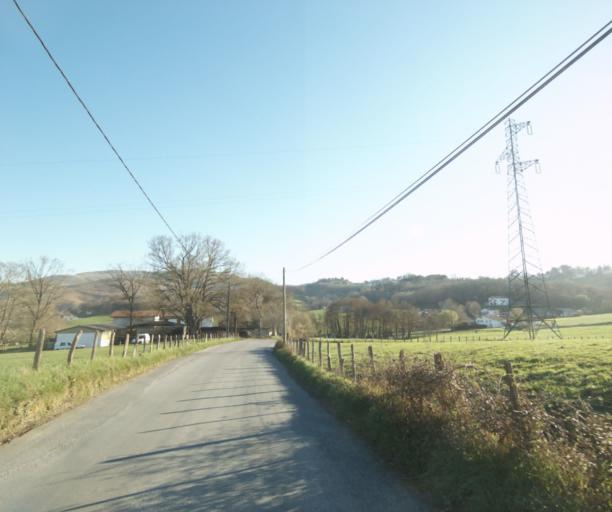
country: FR
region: Aquitaine
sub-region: Departement des Pyrenees-Atlantiques
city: Urrugne
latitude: 43.3562
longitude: -1.7254
